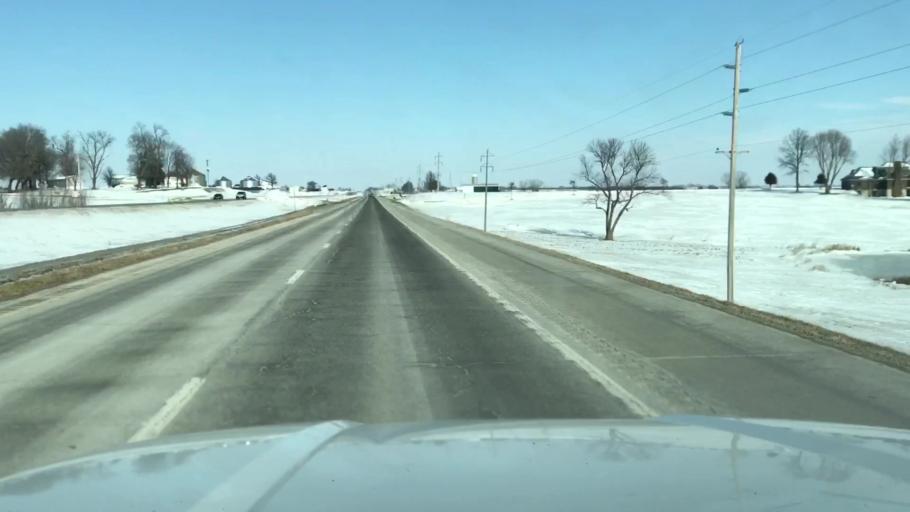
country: US
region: Missouri
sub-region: Nodaway County
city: Maryville
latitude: 40.2372
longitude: -94.8675
